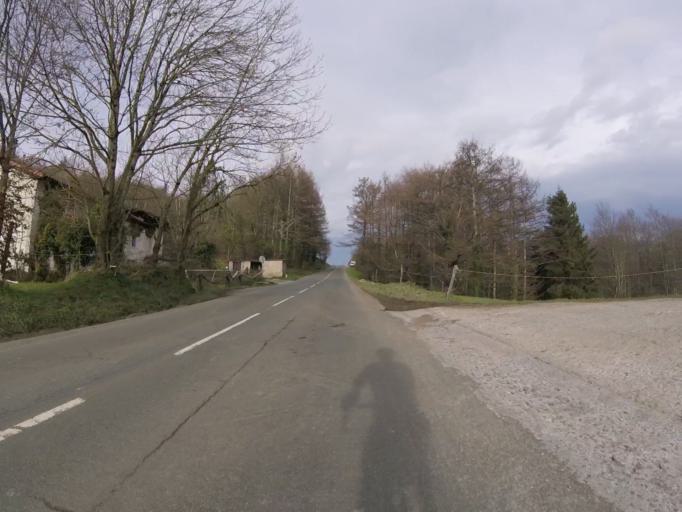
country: ES
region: Basque Country
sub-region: Provincia de Guipuzcoa
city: Errezil
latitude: 43.1461
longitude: -2.1782
